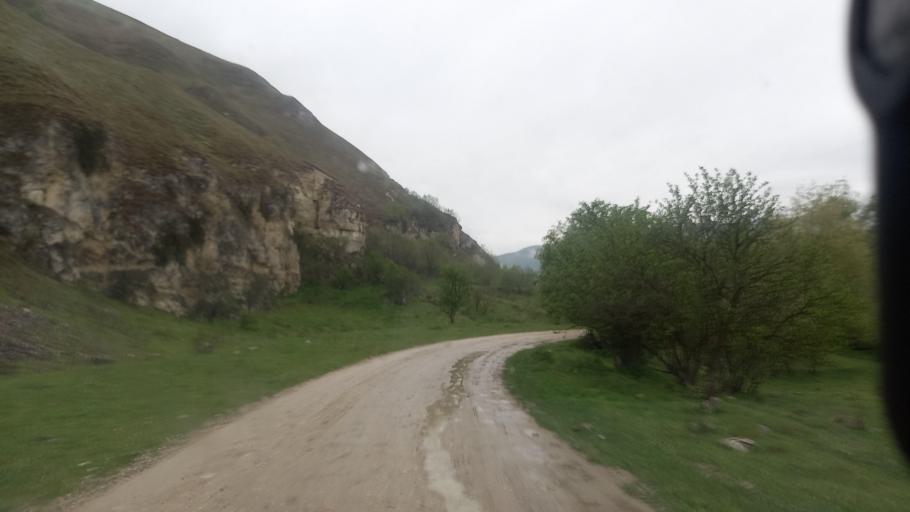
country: RU
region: Kabardino-Balkariya
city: Gundelen
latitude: 43.5966
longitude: 43.0715
